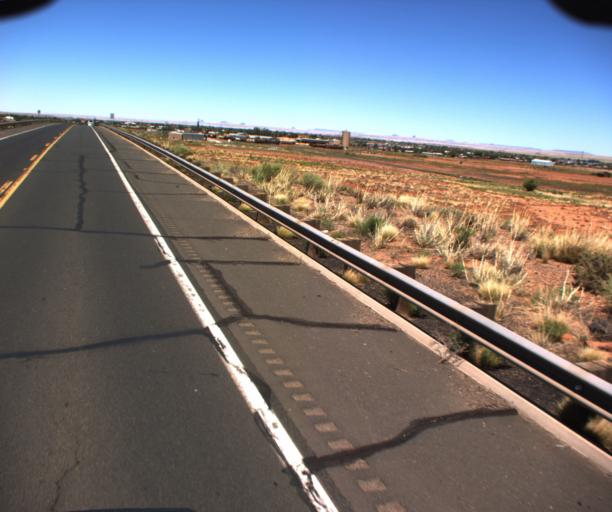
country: US
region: Arizona
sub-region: Navajo County
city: Winslow
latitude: 35.0088
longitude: -110.7035
